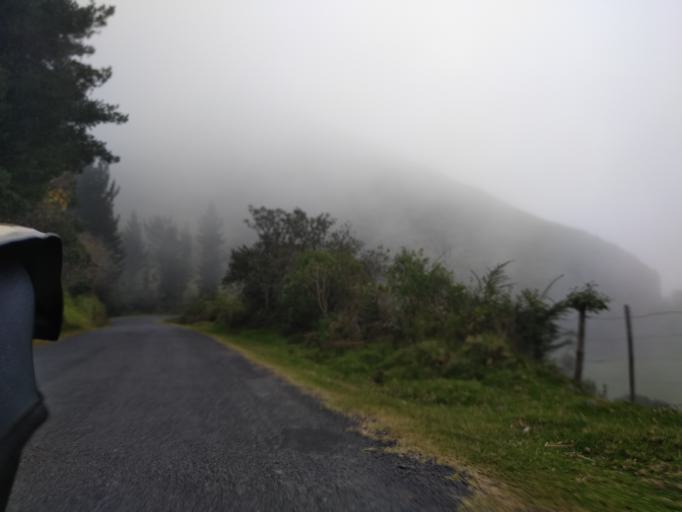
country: EC
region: Cotopaxi
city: Saquisili
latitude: -0.6864
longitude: -78.8334
